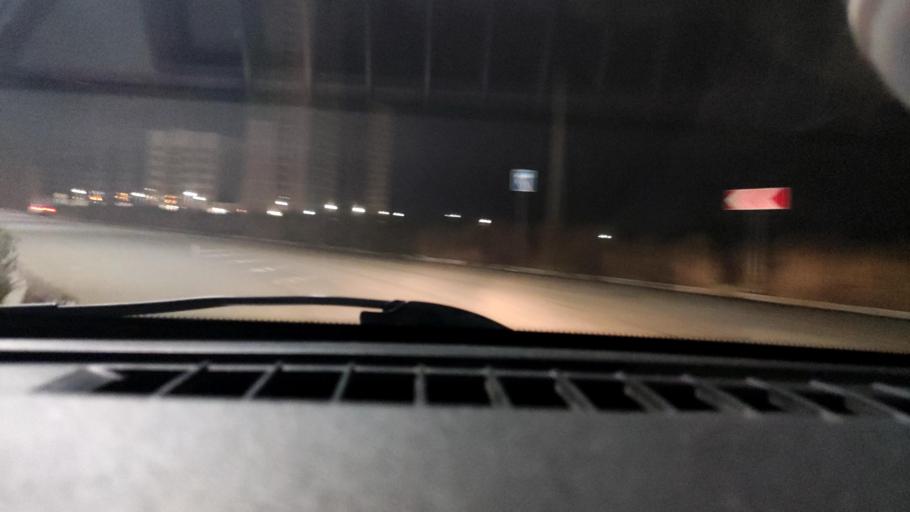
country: RU
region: Samara
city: Samara
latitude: 53.1378
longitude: 50.1689
